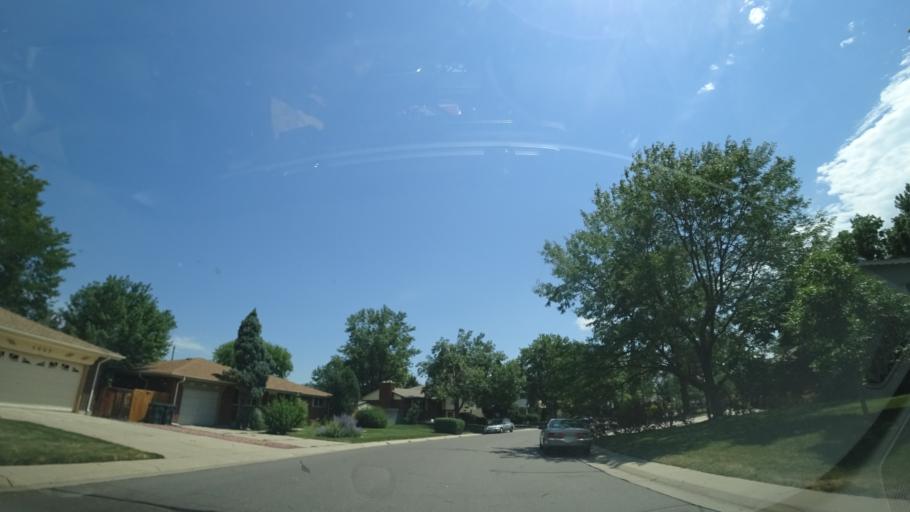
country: US
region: Colorado
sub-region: Jefferson County
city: Lakewood
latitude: 39.6906
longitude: -105.0950
